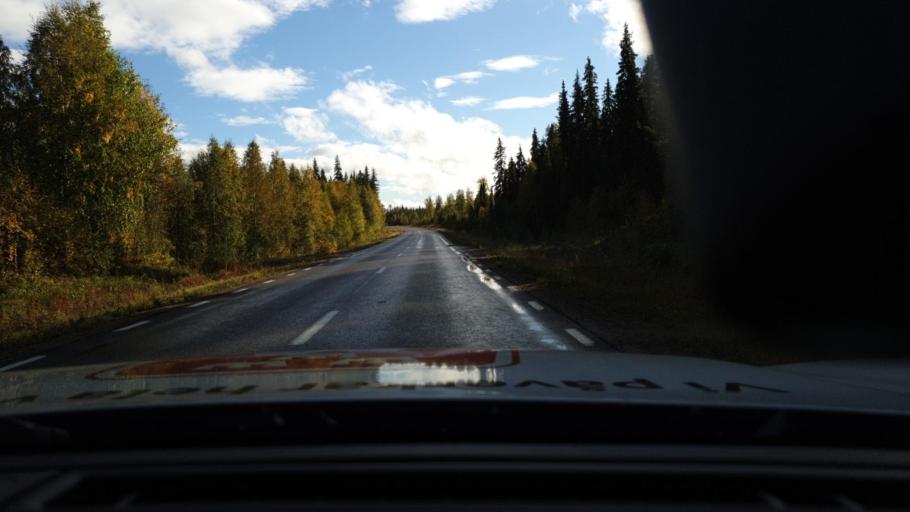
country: SE
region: Norrbotten
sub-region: Overkalix Kommun
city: OEverkalix
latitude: 66.7595
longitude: 22.6783
